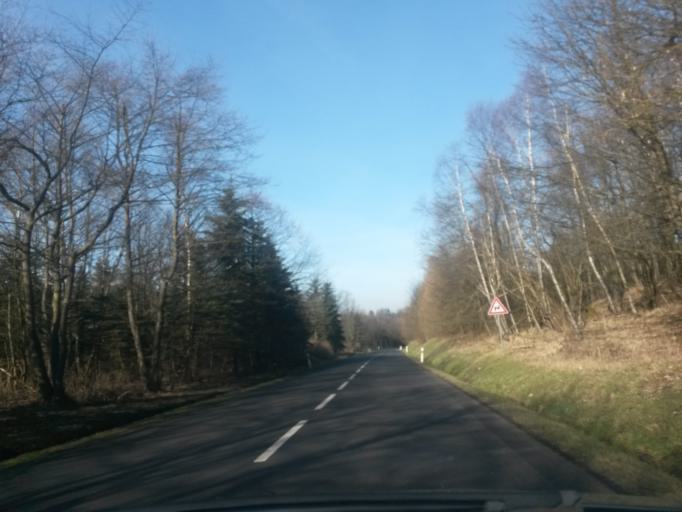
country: CZ
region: Ustecky
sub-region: Okres Chomutov
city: Klasterec nad Ohri
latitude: 50.4539
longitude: 13.1593
